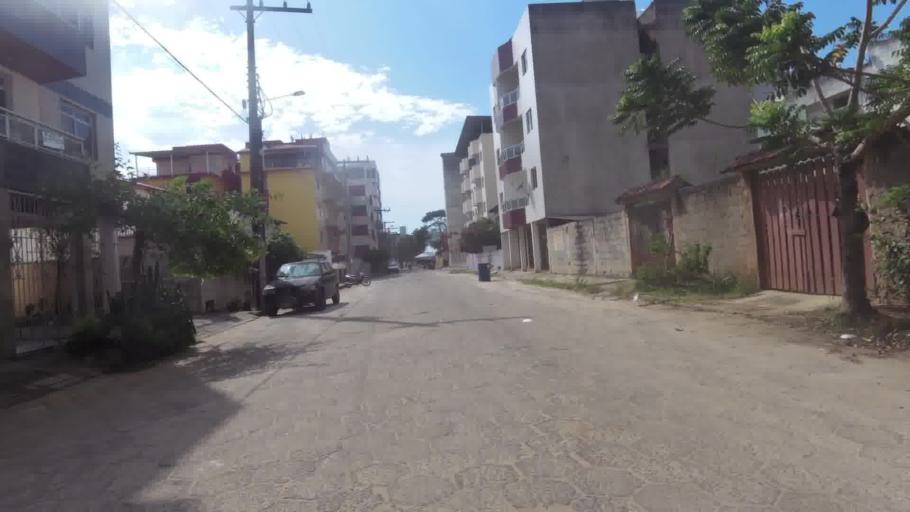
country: BR
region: Espirito Santo
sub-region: Piuma
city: Piuma
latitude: -20.8466
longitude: -40.7433
